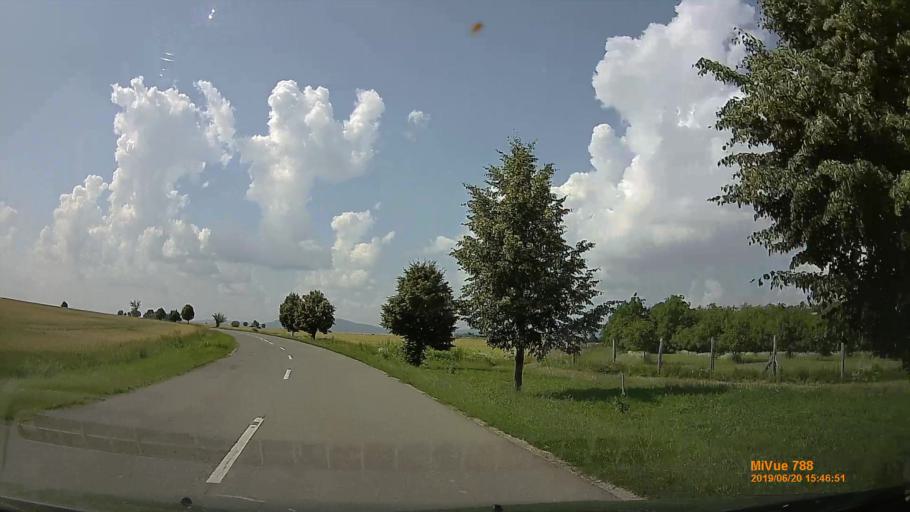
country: HU
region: Baranya
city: Kozarmisleny
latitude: 46.0017
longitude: 18.2411
